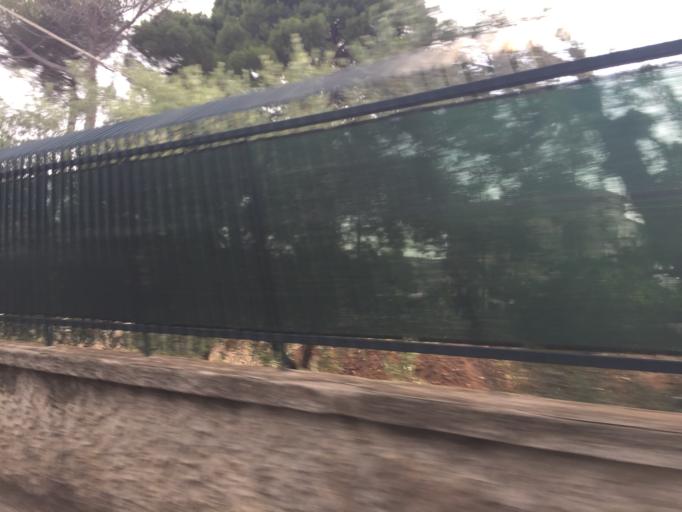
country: IT
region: Apulia
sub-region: Provincia di Bari
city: Capurso
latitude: 41.0529
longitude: 16.9215
